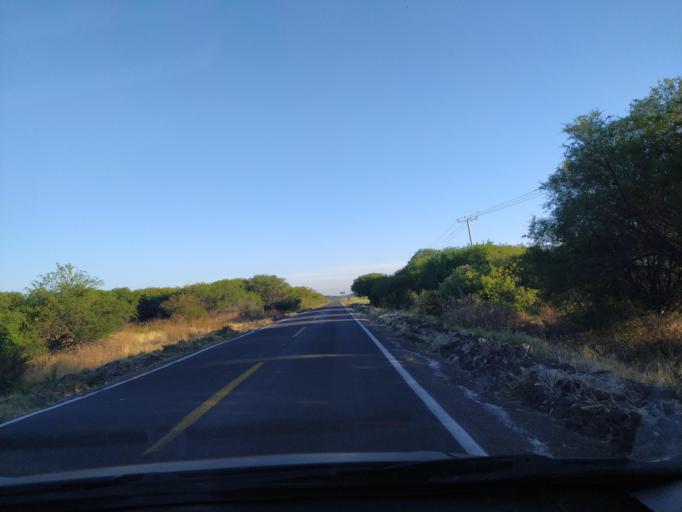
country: MX
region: Guanajuato
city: Ciudad Manuel Doblado
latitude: 20.7757
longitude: -101.8321
